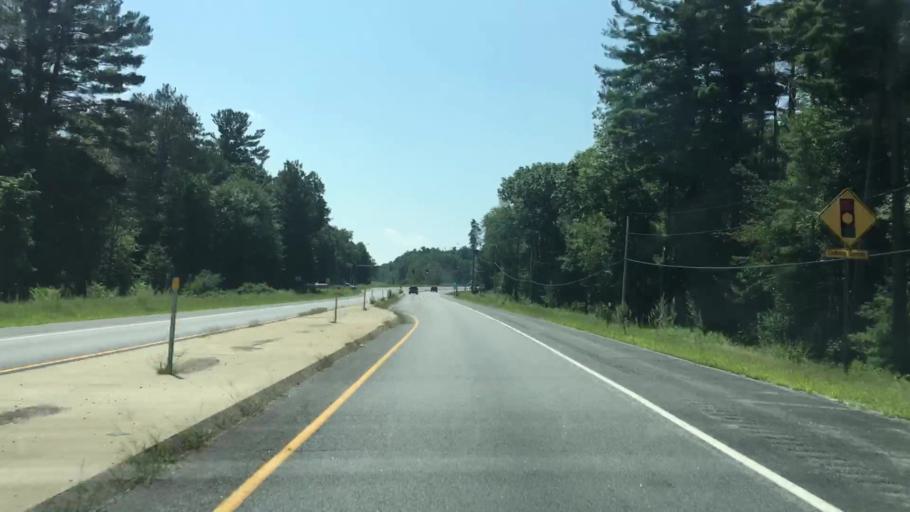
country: US
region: New Hampshire
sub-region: Rockingham County
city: Salem
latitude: 42.8375
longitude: -71.2302
